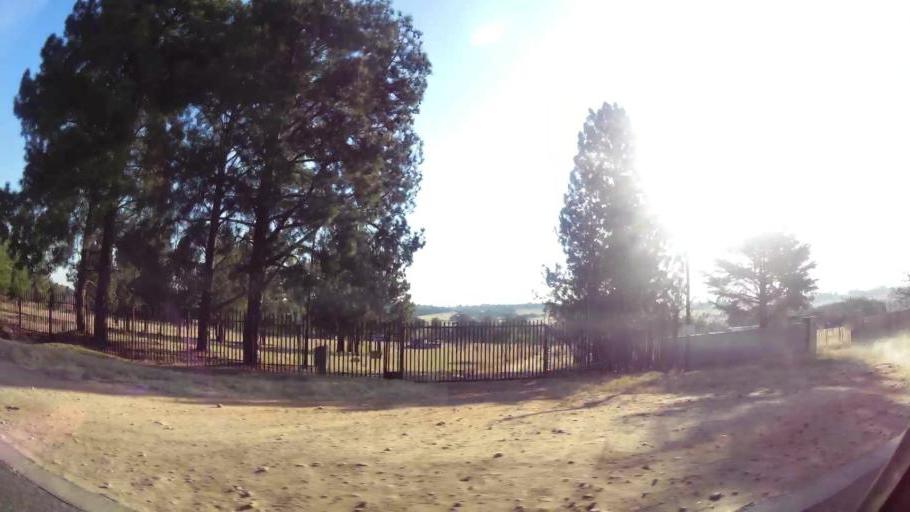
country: ZA
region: Gauteng
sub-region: West Rand District Municipality
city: Muldersdriseloop
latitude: -26.0273
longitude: 27.9085
